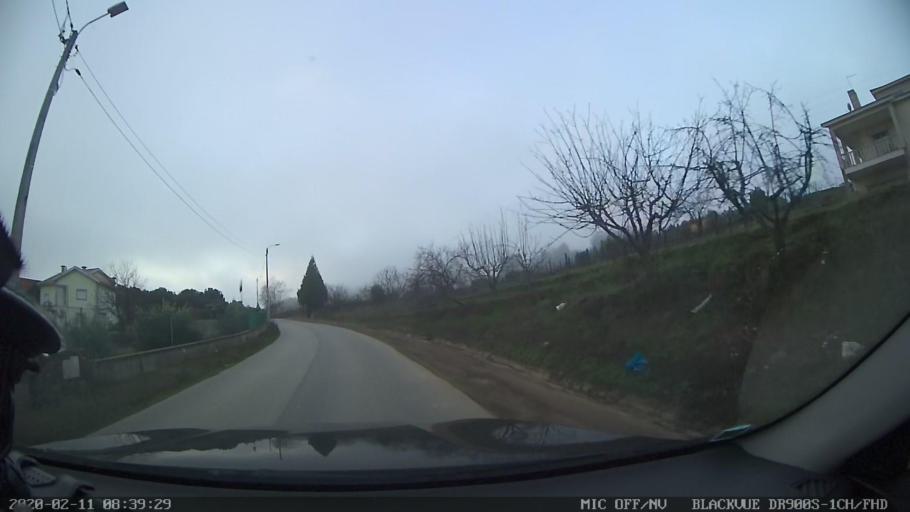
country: PT
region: Vila Real
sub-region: Sabrosa
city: Sabrosa
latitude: 41.2415
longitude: -7.5701
